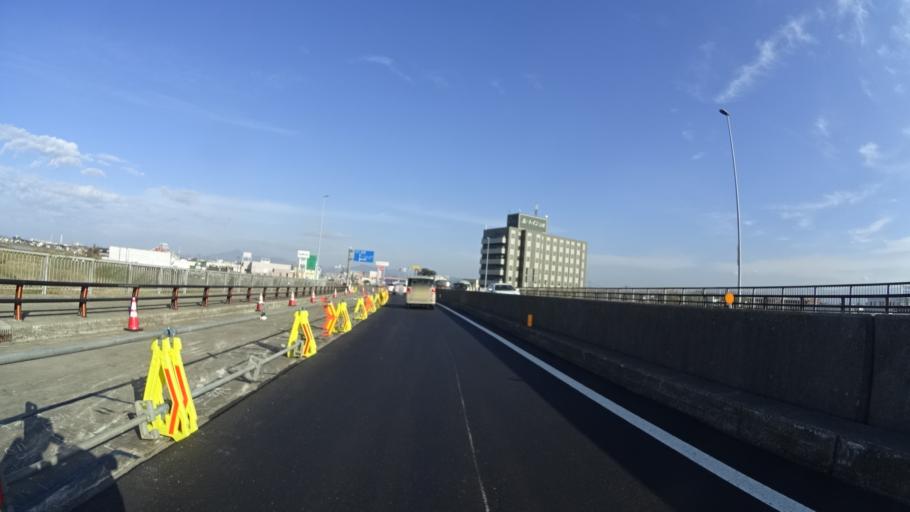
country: JP
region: Niigata
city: Joetsu
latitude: 37.1618
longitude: 138.2464
